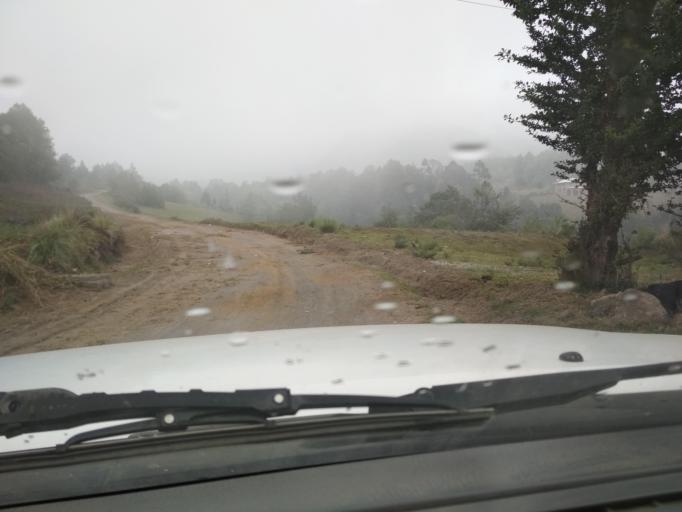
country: MX
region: Veracruz
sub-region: La Perla
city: Chilapa
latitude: 19.0001
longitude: -97.1825
